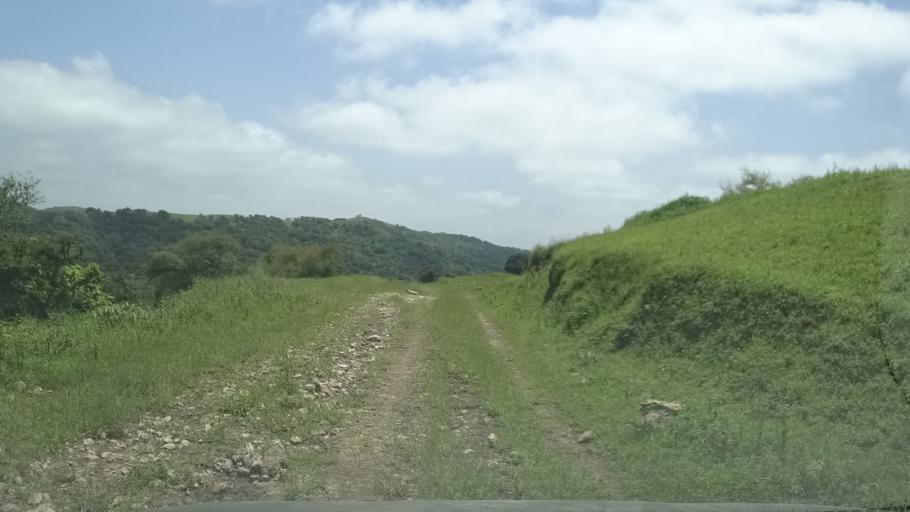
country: OM
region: Zufar
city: Salalah
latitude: 17.2184
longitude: 54.2563
